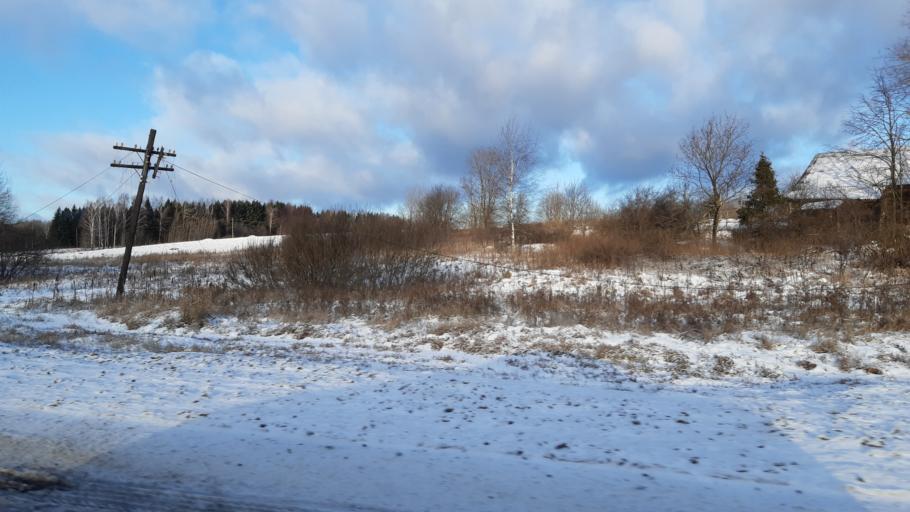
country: RU
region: Moskovskaya
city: Svatkovo
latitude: 56.3108
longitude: 38.3188
